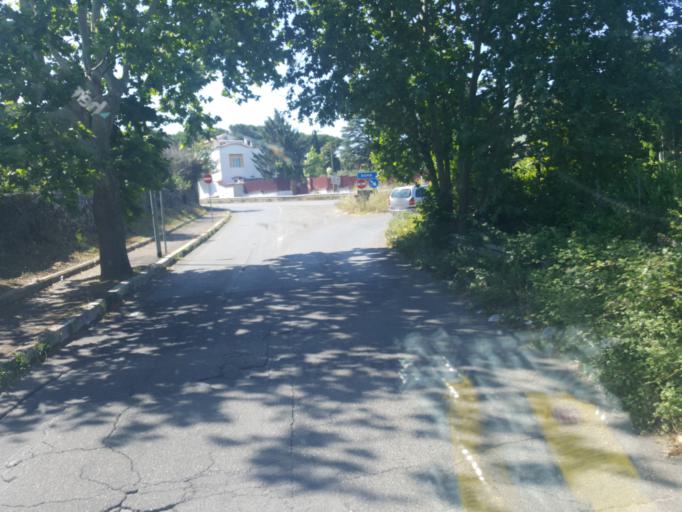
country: IT
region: Latium
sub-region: Citta metropolitana di Roma Capitale
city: Frascati
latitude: 41.8219
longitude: 12.6442
